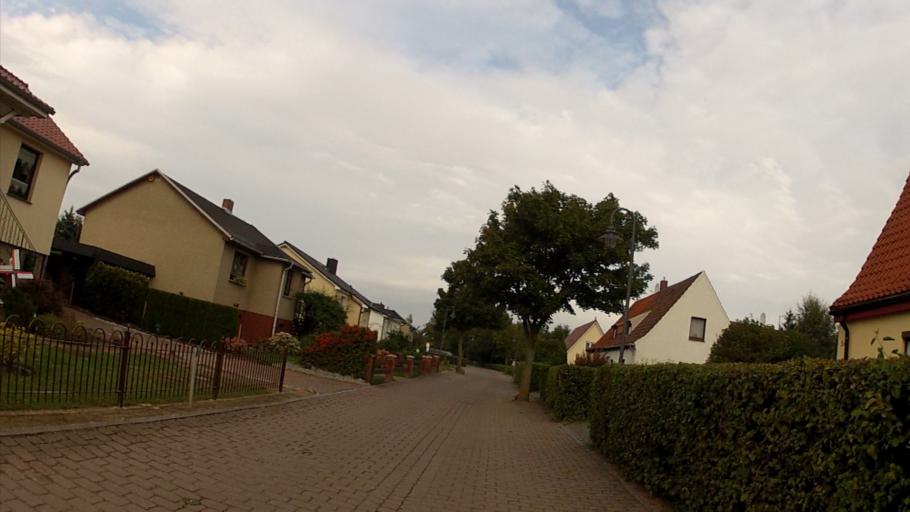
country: DE
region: Mecklenburg-Vorpommern
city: Bastorf
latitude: 54.1092
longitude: 11.6244
